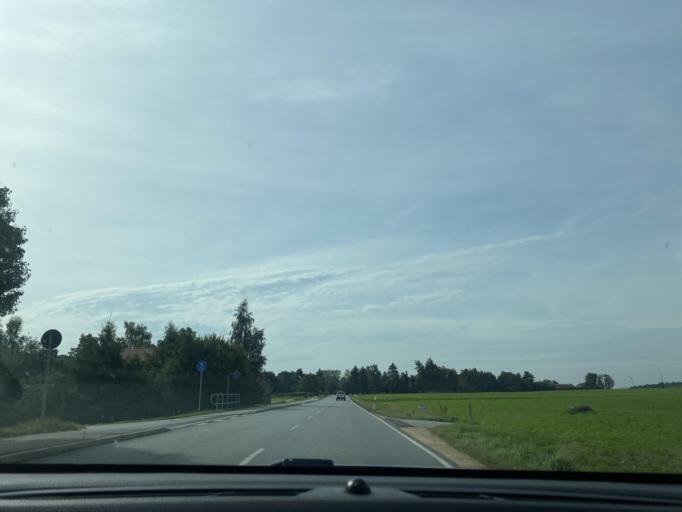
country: DE
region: Saxony
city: Quitzdorf
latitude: 51.2136
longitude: 14.7692
